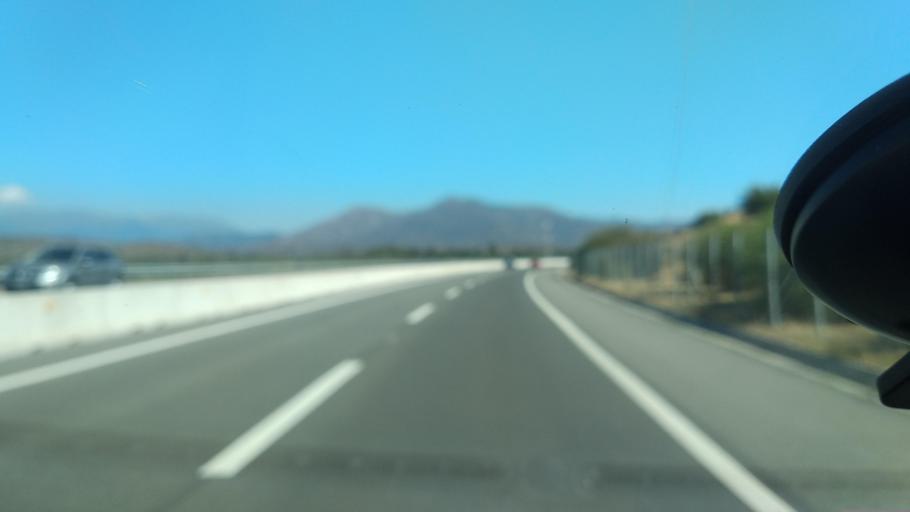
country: CL
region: Valparaiso
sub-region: Provincia de Marga Marga
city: Limache
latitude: -33.0151
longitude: -71.3211
